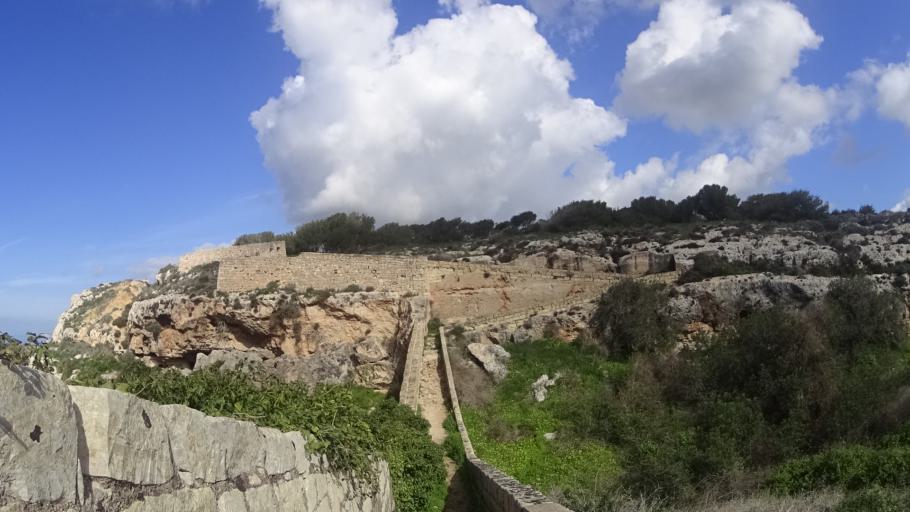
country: MT
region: L-Imgarr
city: Imgarr
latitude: 35.9033
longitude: 14.3789
